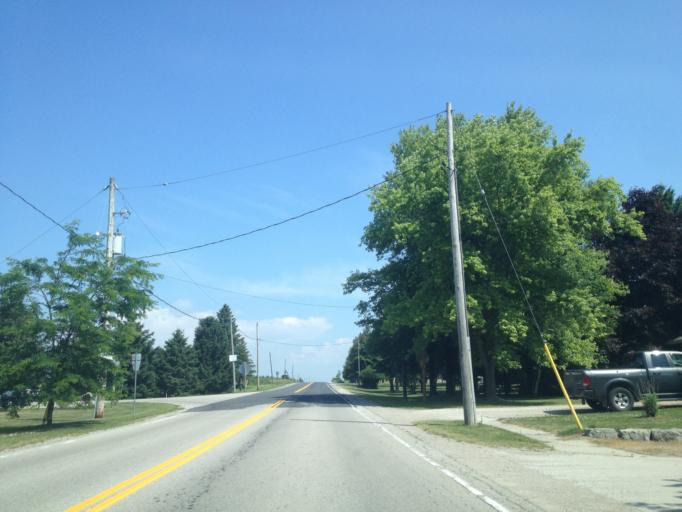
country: CA
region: Ontario
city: Huron East
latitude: 43.3914
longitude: -81.2222
